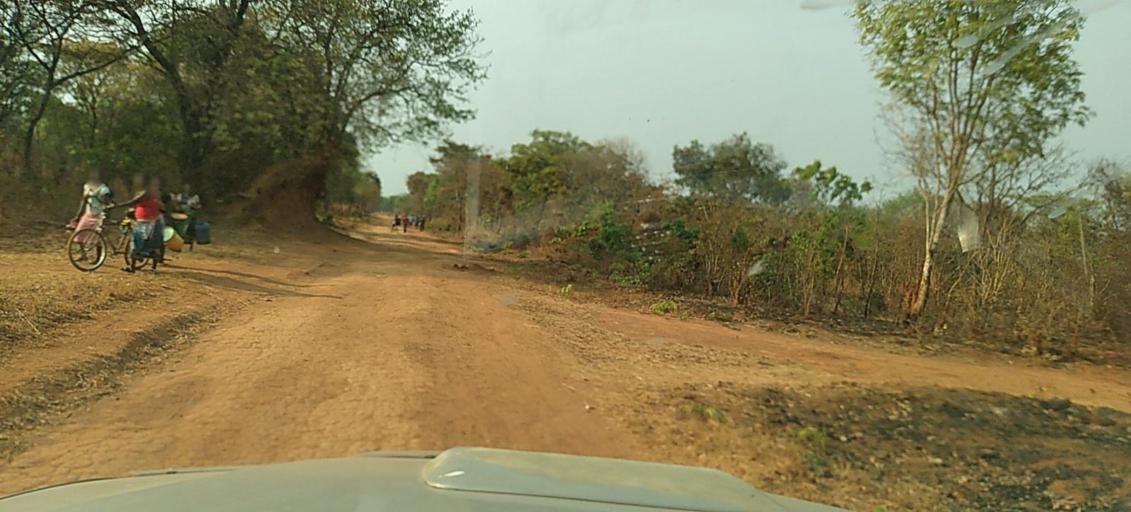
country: ZM
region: North-Western
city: Kasempa
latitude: -13.2995
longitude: 26.5541
